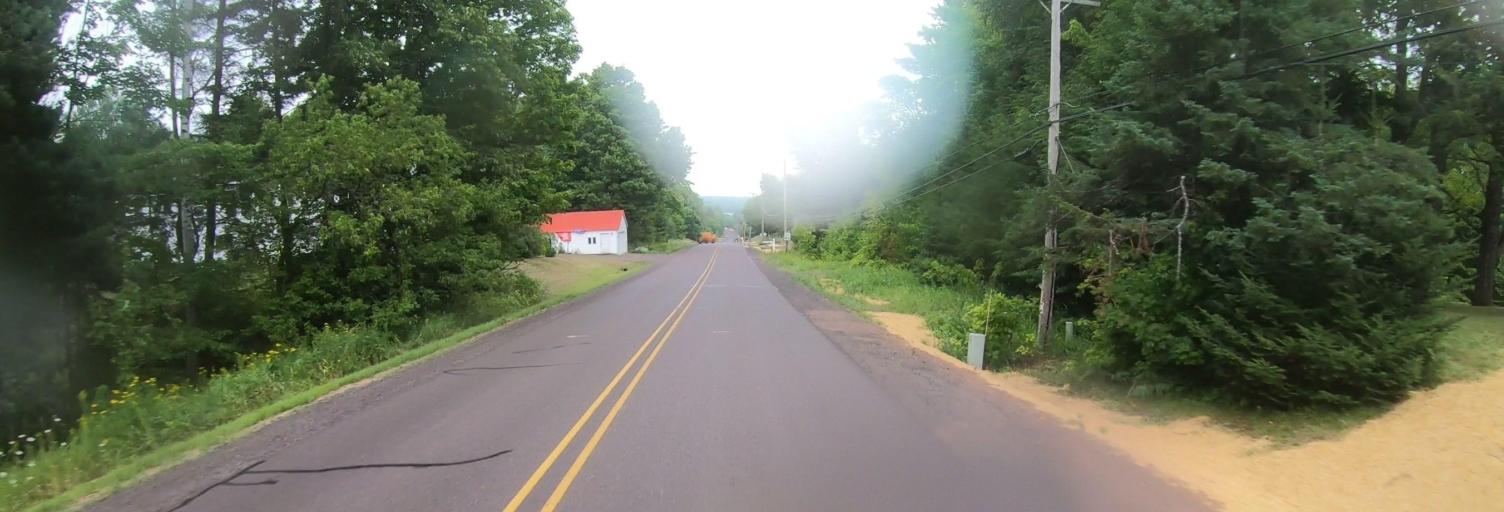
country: US
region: Michigan
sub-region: Houghton County
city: Dollar Bay
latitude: 47.0254
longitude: -88.5371
